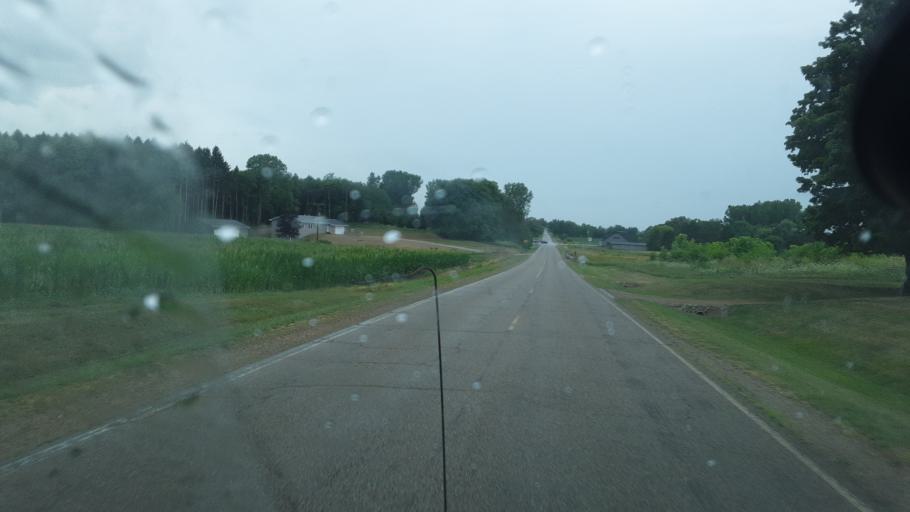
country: US
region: Michigan
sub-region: Hillsdale County
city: Reading
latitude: 41.7081
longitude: -84.7456
